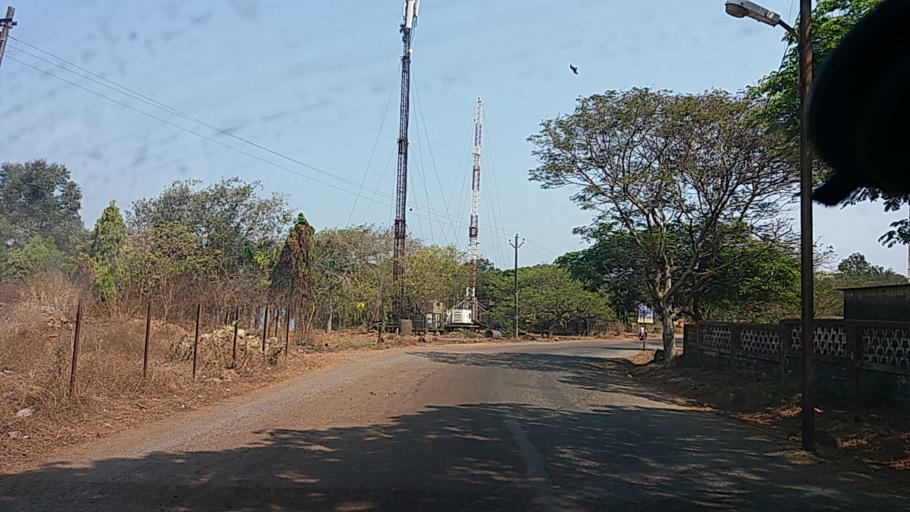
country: IN
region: Goa
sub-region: South Goa
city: Marmagao
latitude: 15.4060
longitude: 73.7890
